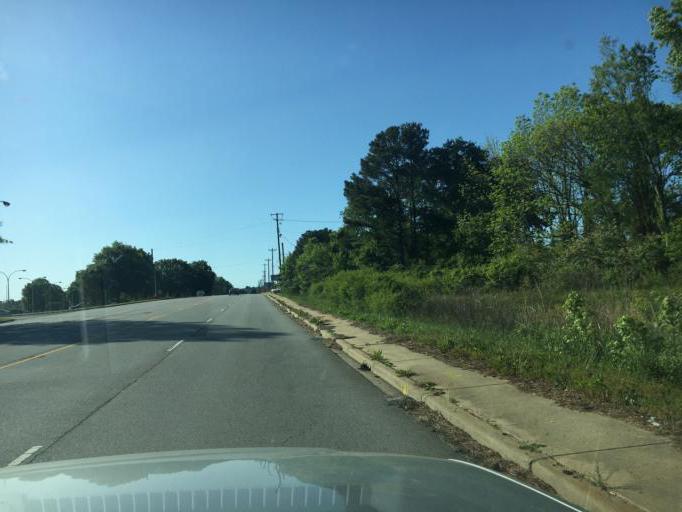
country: US
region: South Carolina
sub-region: Lexington County
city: Seven Oaks
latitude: 34.0482
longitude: -81.1536
